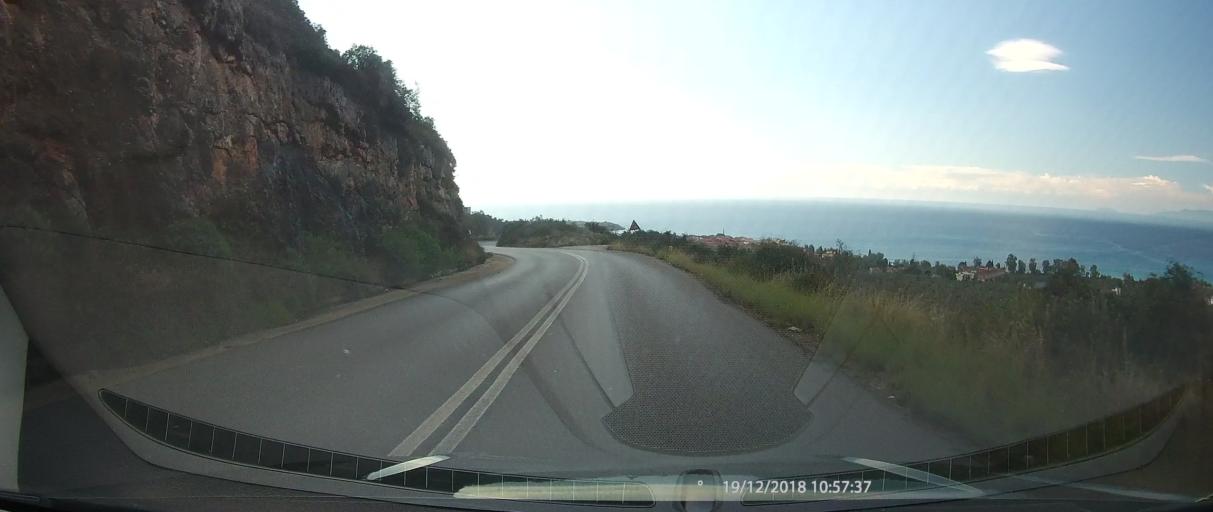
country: GR
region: Peloponnese
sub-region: Nomos Messinias
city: Kardamyli
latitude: 36.8968
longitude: 22.2370
